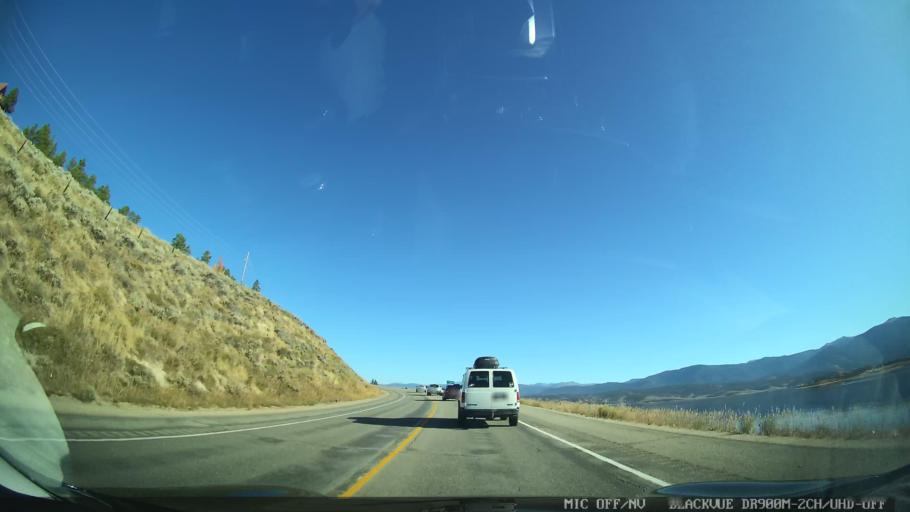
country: US
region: Colorado
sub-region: Grand County
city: Granby
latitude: 40.1494
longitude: -105.8893
